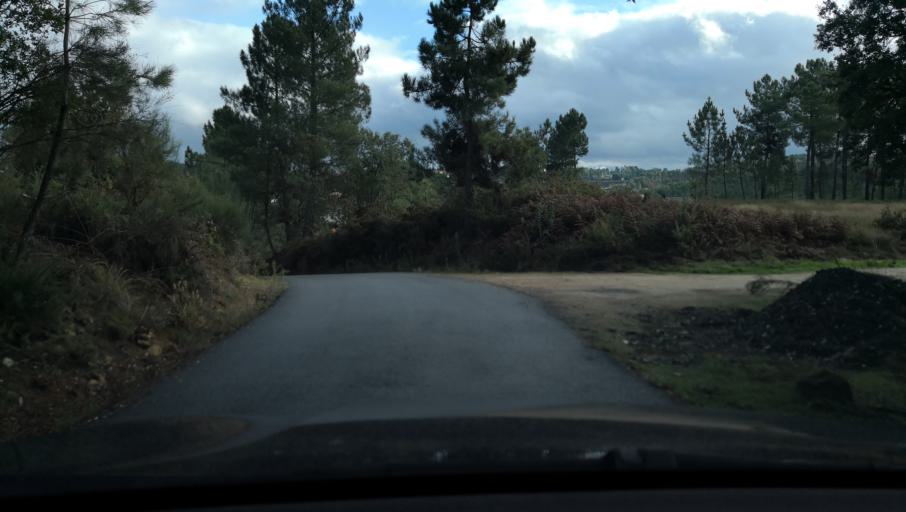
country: PT
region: Vila Real
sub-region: Vila Real
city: Vila Real
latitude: 41.2670
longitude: -7.7170
